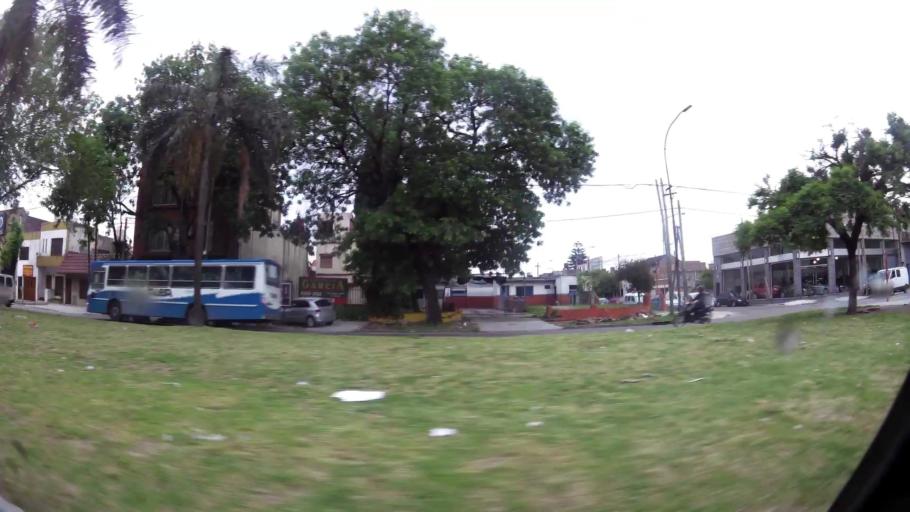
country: AR
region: Buenos Aires
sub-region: Partido de Lanus
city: Lanus
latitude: -34.6835
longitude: -58.4008
